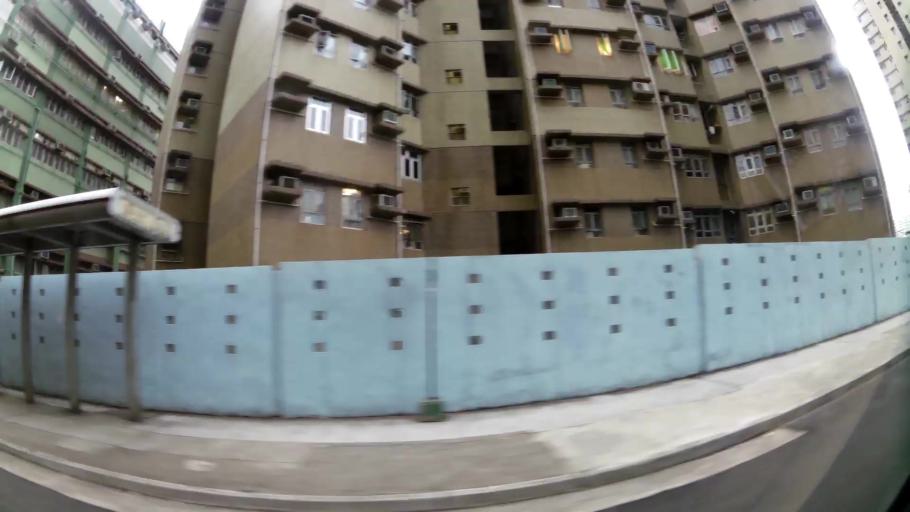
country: HK
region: Tsuen Wan
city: Tsuen Wan
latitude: 22.3639
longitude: 114.1303
